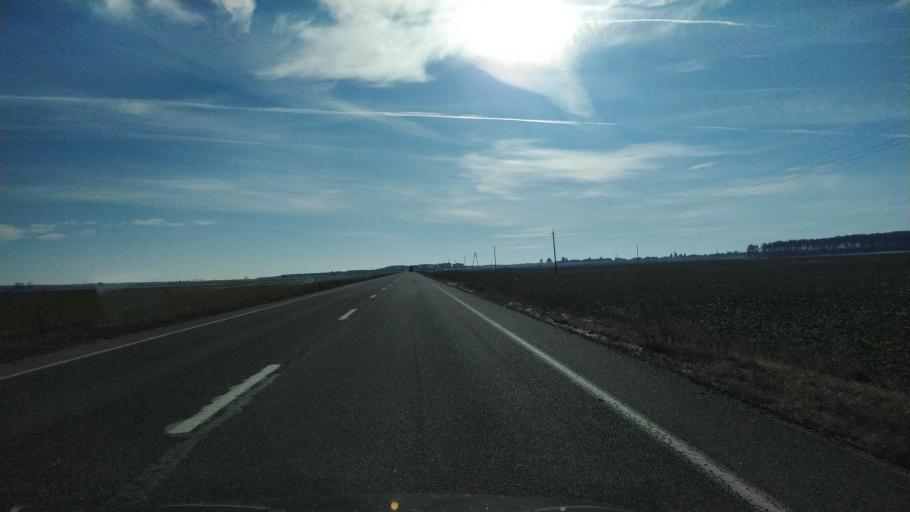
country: BY
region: Brest
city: Kamyanyets
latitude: 52.4191
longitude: 23.8447
